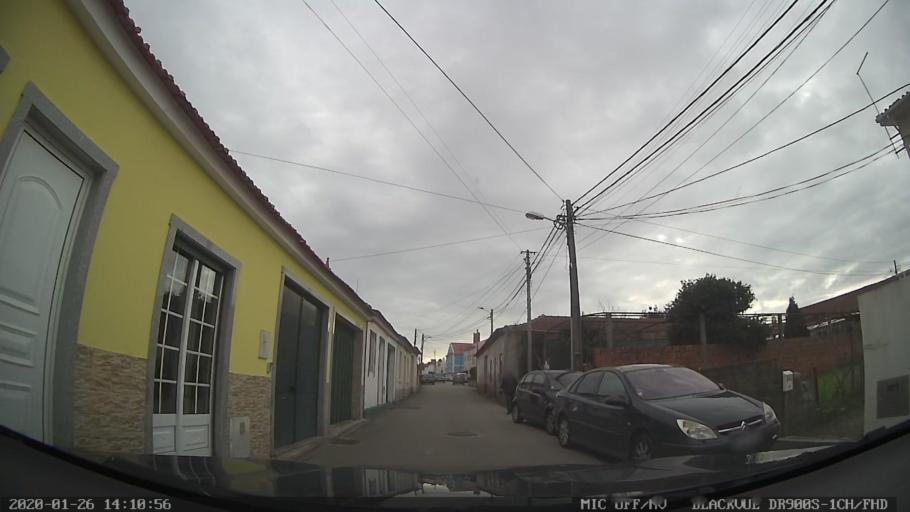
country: PT
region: Aveiro
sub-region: Aveiro
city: Aradas
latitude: 40.6300
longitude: -8.6258
